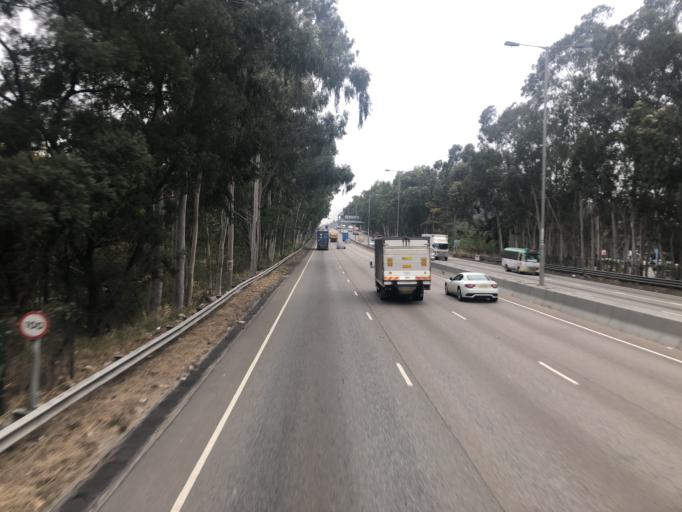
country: CN
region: Guangdong
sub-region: Shenzhen
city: Shenzhen
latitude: 22.4946
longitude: 114.0727
